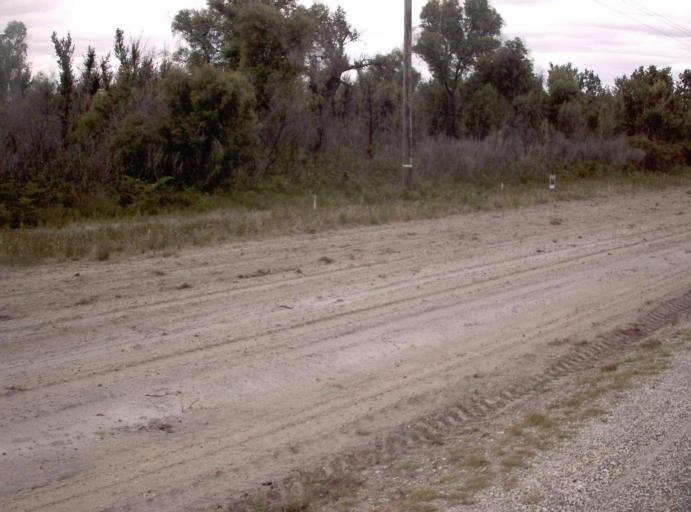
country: AU
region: Victoria
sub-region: East Gippsland
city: Bairnsdale
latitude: -38.0979
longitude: 147.5087
